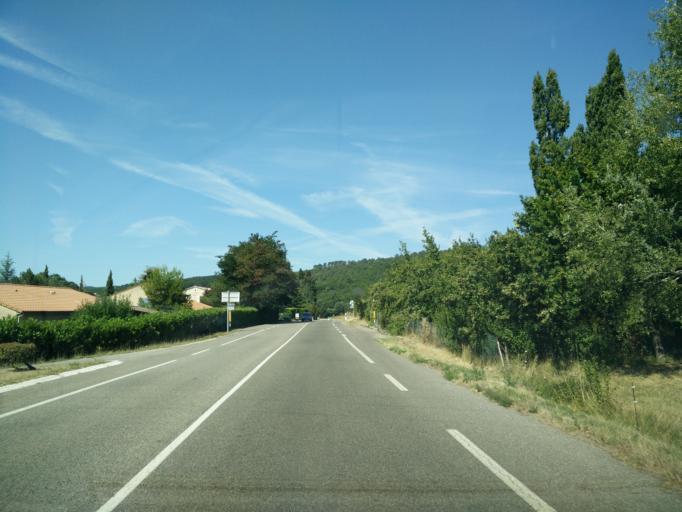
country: FR
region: Rhone-Alpes
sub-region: Departement de la Drome
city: Dieulefit
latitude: 44.5316
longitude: 5.0040
